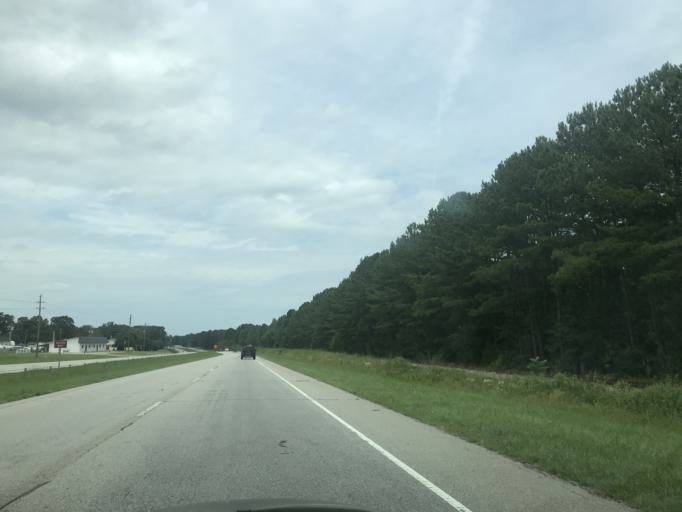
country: US
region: North Carolina
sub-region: Franklin County
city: Franklinton
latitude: 36.1298
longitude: -78.4509
